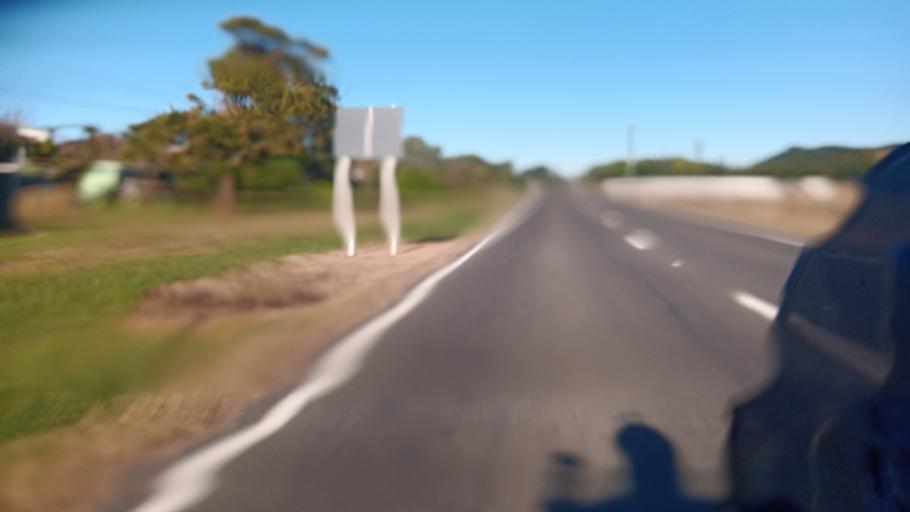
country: NZ
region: Hawke's Bay
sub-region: Napier City
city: Napier
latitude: -39.3691
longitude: 176.8969
